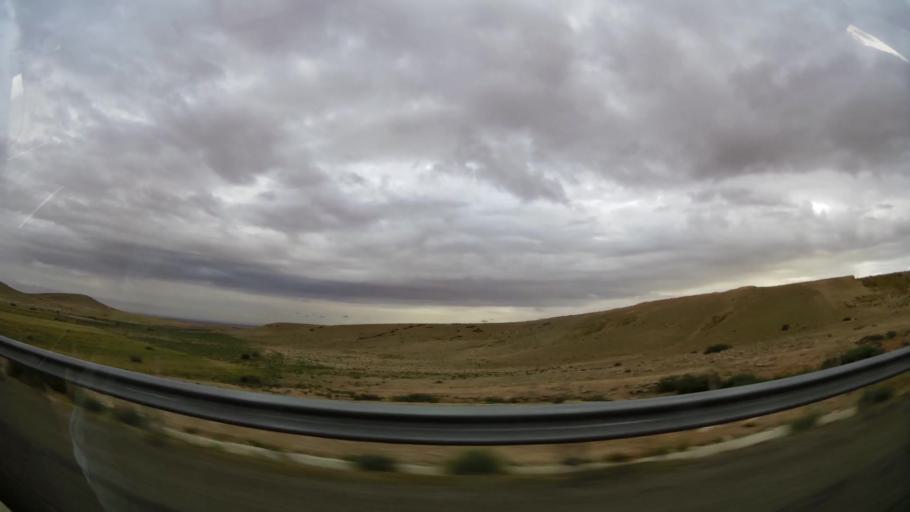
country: MA
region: Taza-Al Hoceima-Taounate
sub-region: Taza
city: Guercif
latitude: 34.3029
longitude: -3.6705
